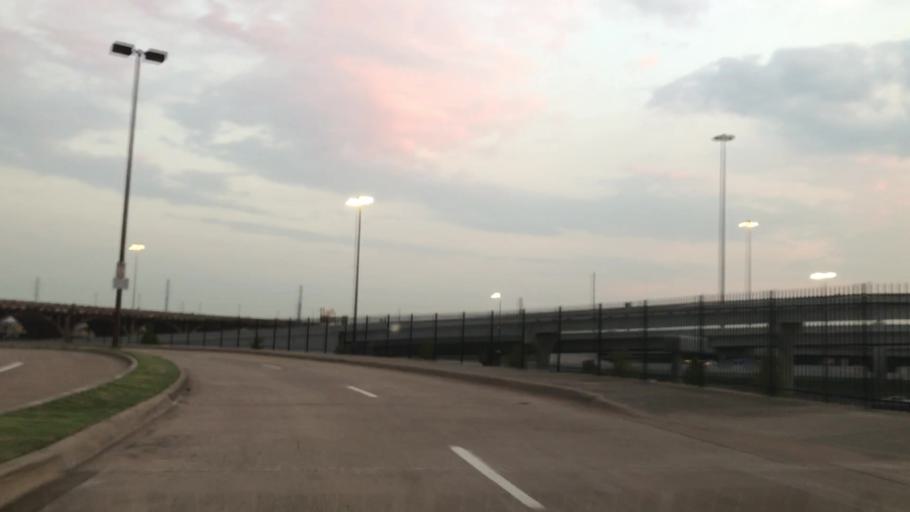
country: US
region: Texas
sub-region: Dallas County
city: Dallas
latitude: 32.7727
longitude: -96.8091
